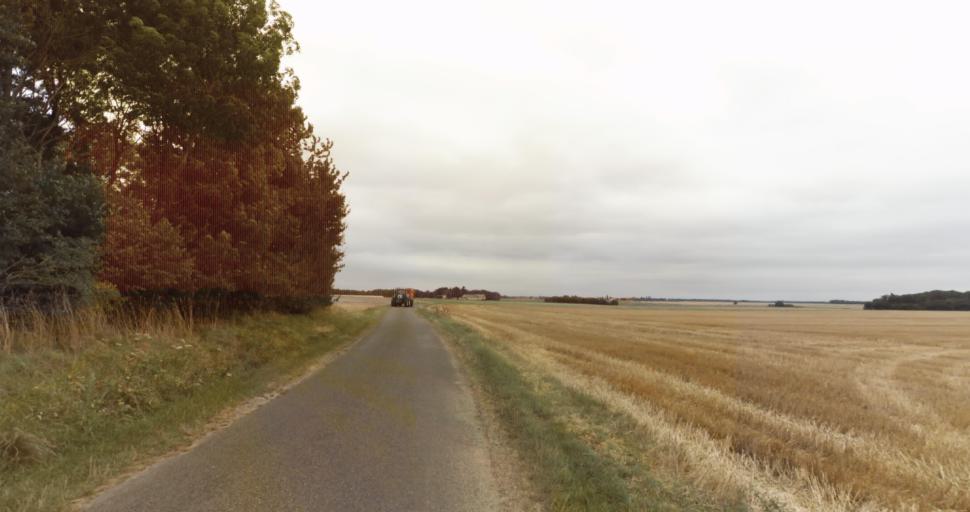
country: FR
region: Haute-Normandie
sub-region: Departement de l'Eure
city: La Couture-Boussey
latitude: 48.9239
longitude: 1.3601
